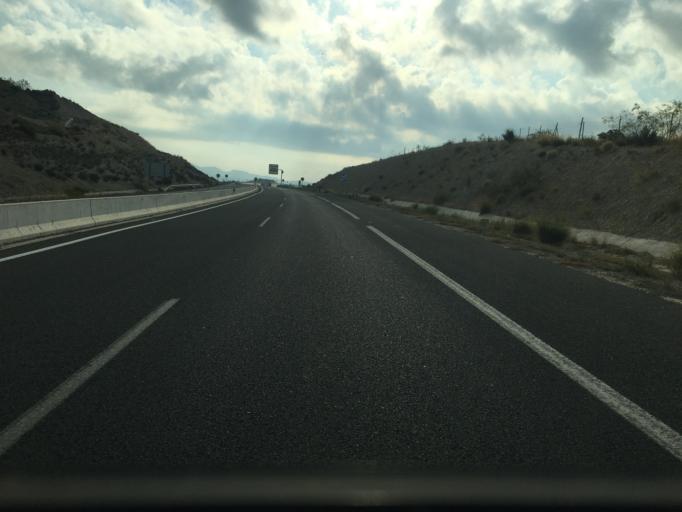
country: ES
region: Murcia
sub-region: Murcia
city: Beniel
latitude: 37.9954
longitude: -0.9938
